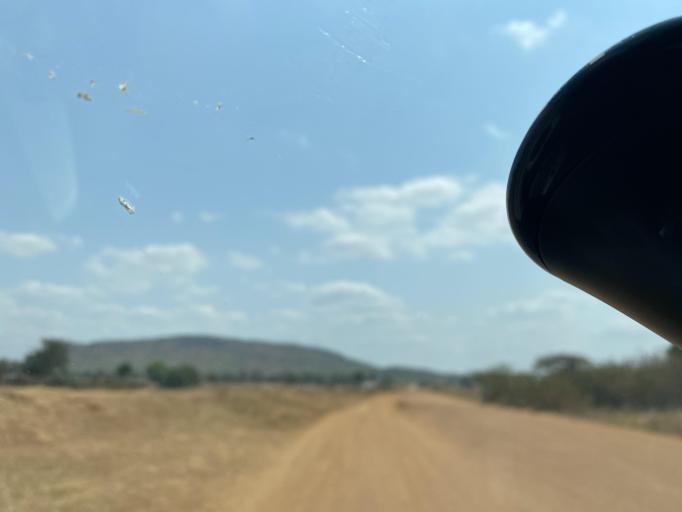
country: ZM
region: Lusaka
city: Chongwe
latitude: -15.5954
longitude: 28.7553
